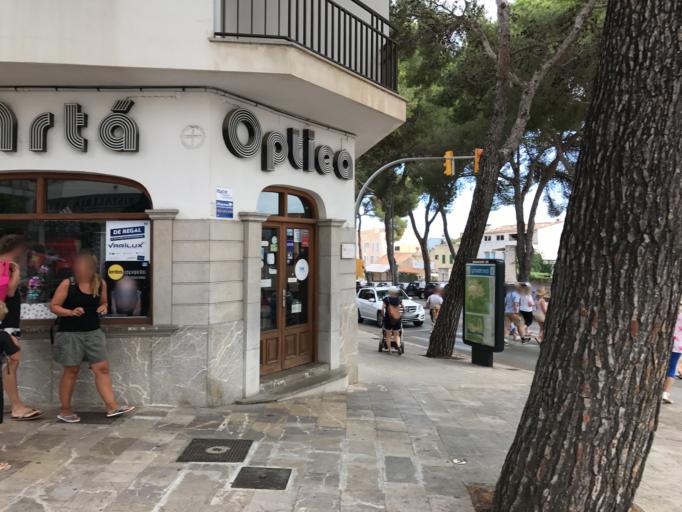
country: ES
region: Balearic Islands
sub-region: Illes Balears
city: Arta
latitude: 39.6913
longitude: 3.3484
